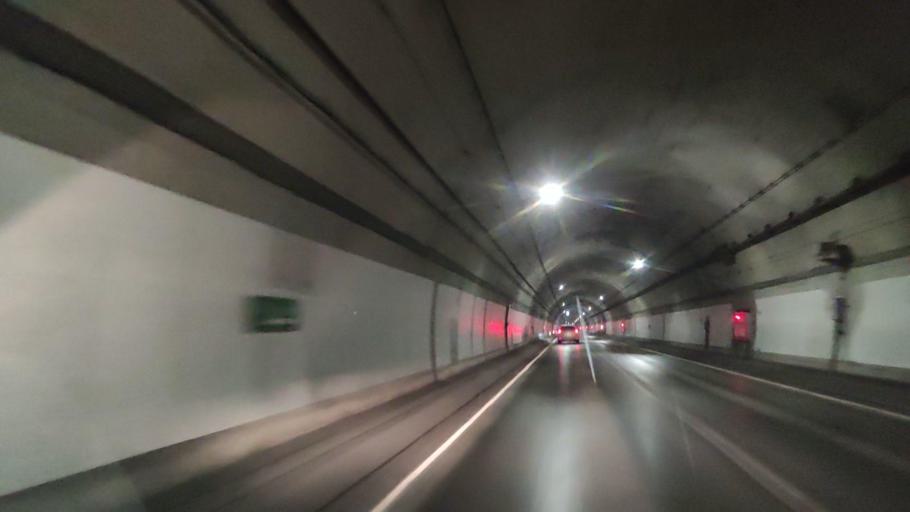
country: JP
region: Hokkaido
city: Rumoi
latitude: 43.7065
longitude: 141.3345
